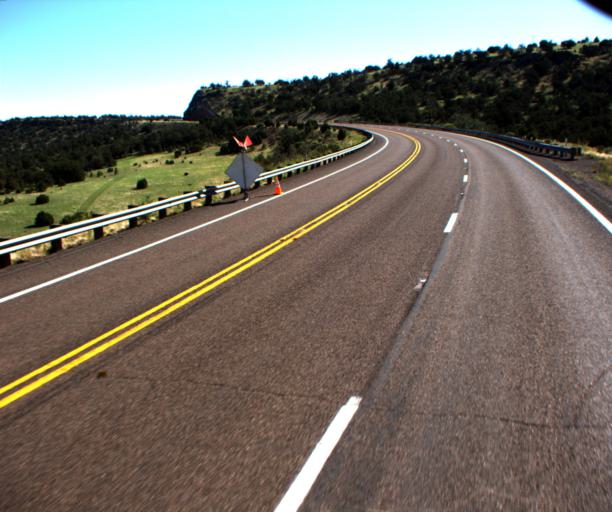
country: US
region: Arizona
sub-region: Apache County
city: Eagar
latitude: 34.0886
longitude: -109.2371
